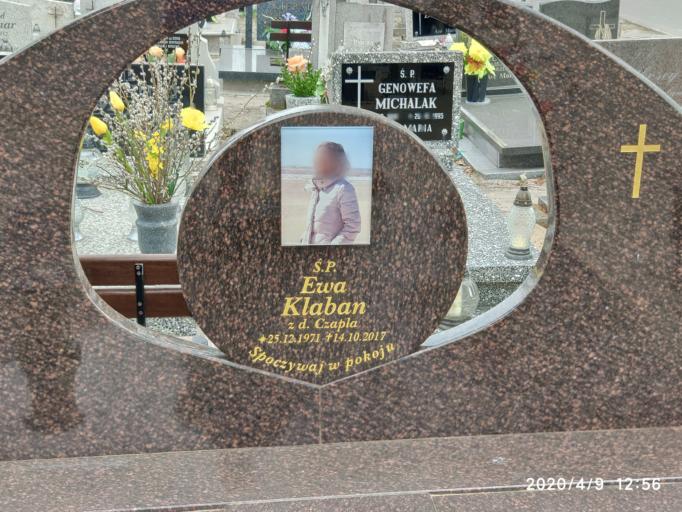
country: PL
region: Lubusz
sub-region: Powiat zielonogorski
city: Sulechow
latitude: 52.0838
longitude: 15.6134
